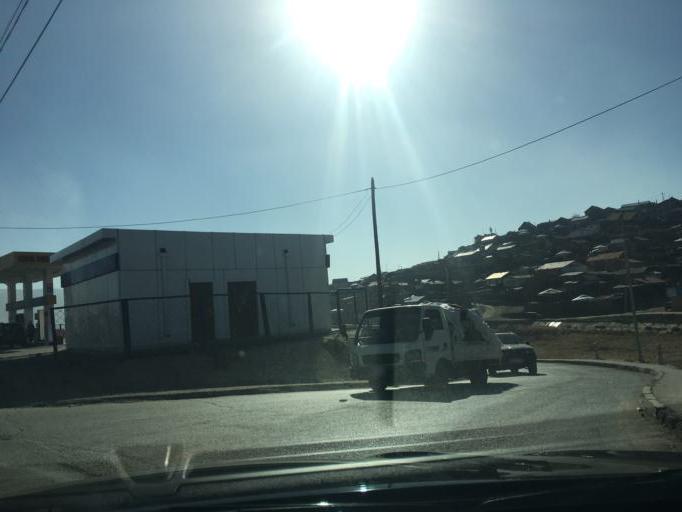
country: MN
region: Ulaanbaatar
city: Ulaanbaatar
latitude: 47.9377
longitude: 106.8835
